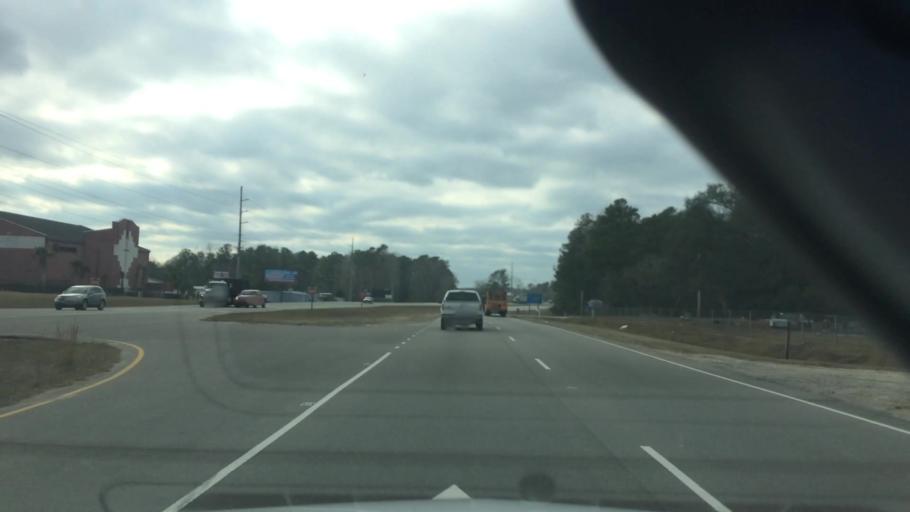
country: US
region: North Carolina
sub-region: Brunswick County
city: Shallotte
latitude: 33.9876
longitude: -78.3585
